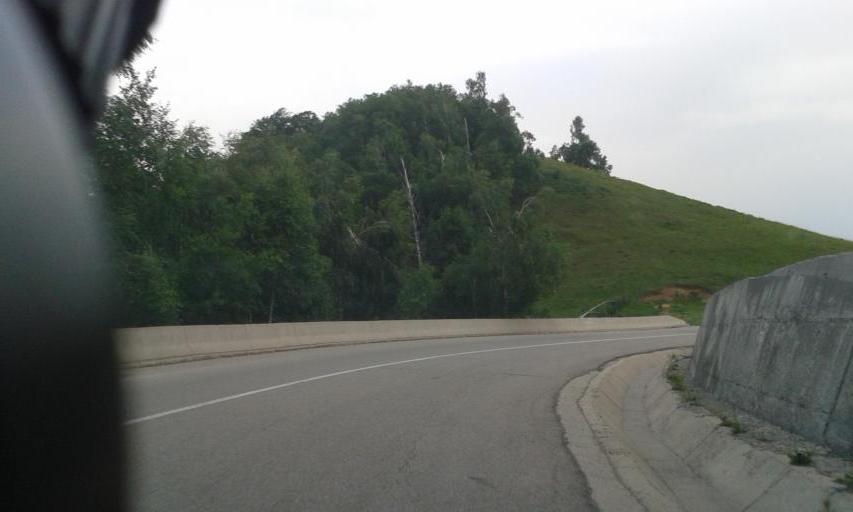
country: RO
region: Gorj
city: Novaci-Straini
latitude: 45.2240
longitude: 23.6964
